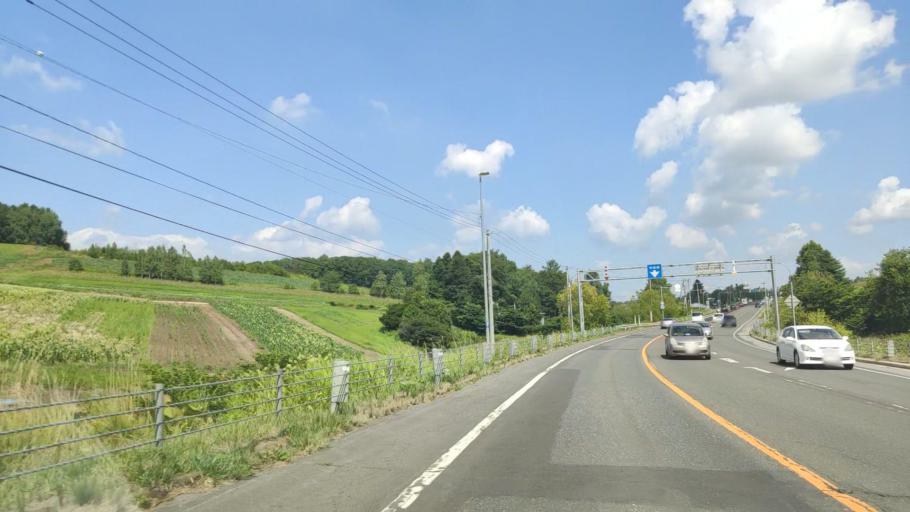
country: JP
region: Hokkaido
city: Shimo-furano
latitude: 43.5370
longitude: 142.4395
